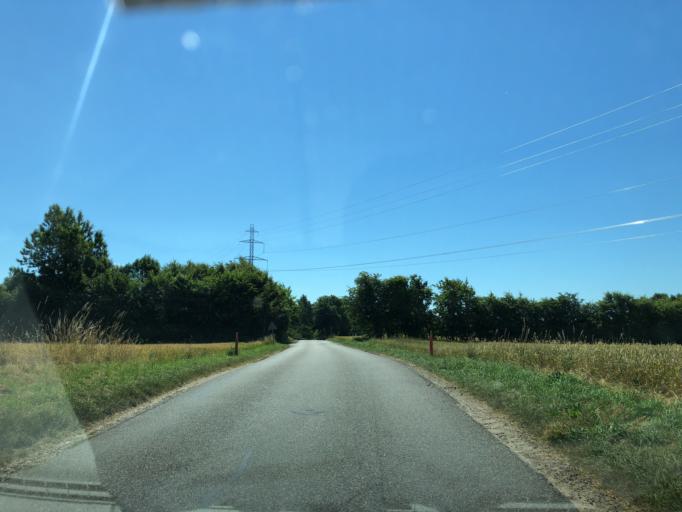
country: DK
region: Central Jutland
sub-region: Viborg Kommune
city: Viborg
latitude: 56.5127
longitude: 9.5068
